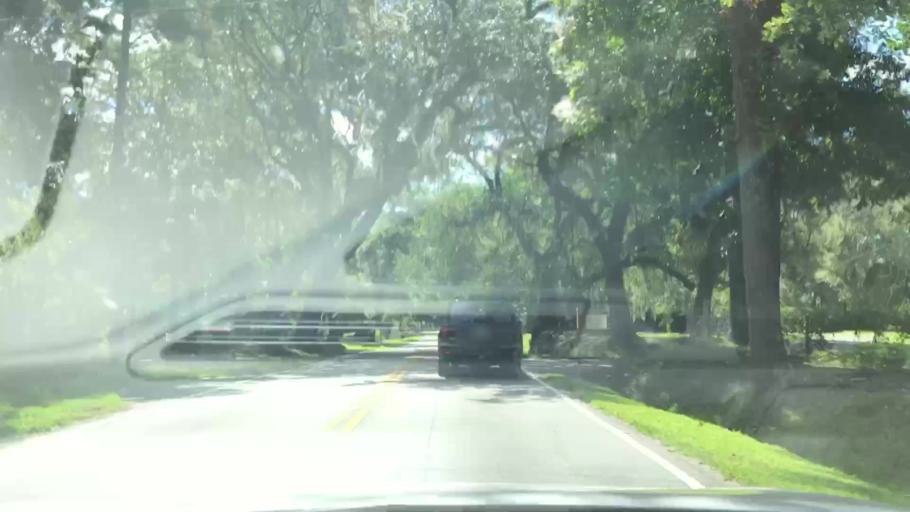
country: US
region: South Carolina
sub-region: Charleston County
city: Shell Point
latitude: 32.8387
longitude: -80.0514
